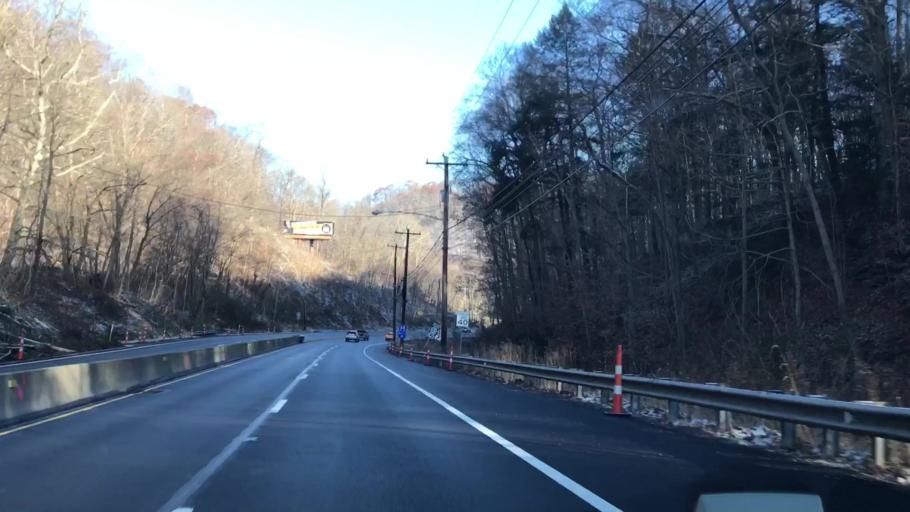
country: US
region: Pennsylvania
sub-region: Allegheny County
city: Sewickley
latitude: 40.5353
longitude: -80.2018
